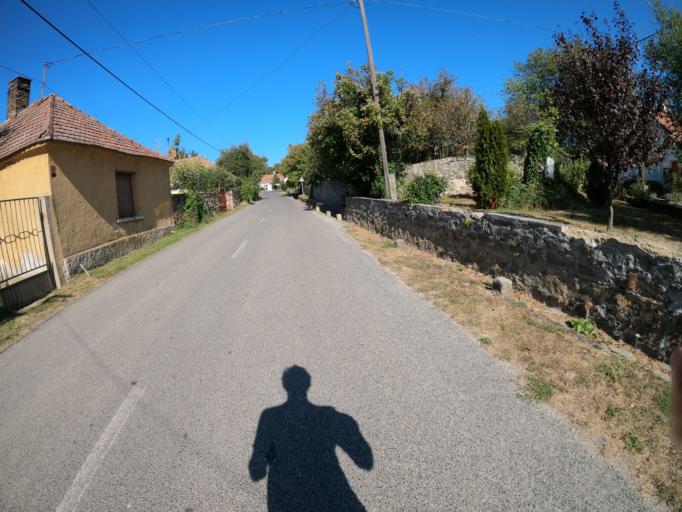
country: HU
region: Veszprem
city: Revfueloep
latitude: 46.8854
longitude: 17.5649
